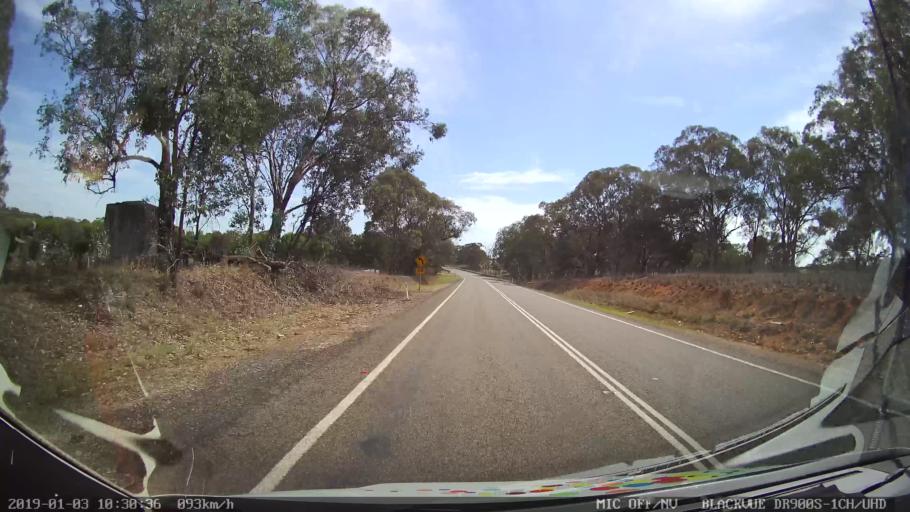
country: AU
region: New South Wales
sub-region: Young
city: Young
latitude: -34.3605
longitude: 148.2701
